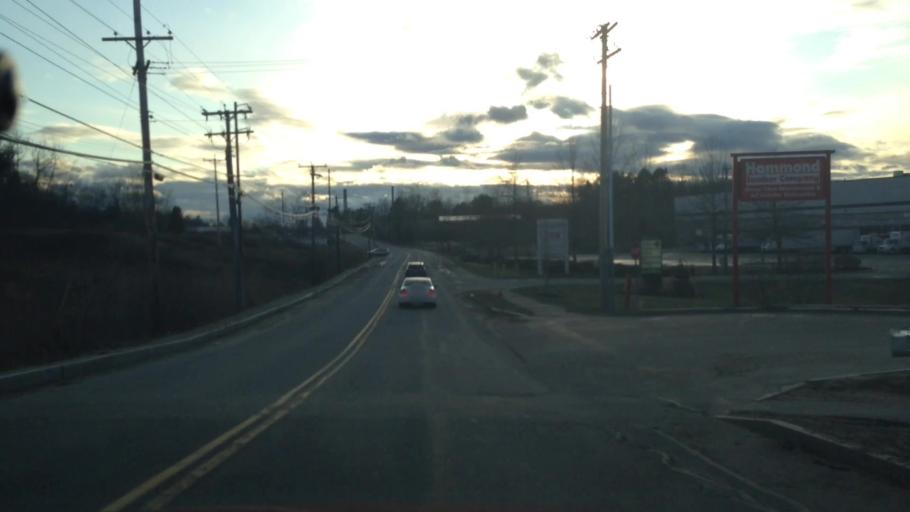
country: US
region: Maine
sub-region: Cumberland County
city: Westbrook
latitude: 43.6862
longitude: -70.3301
